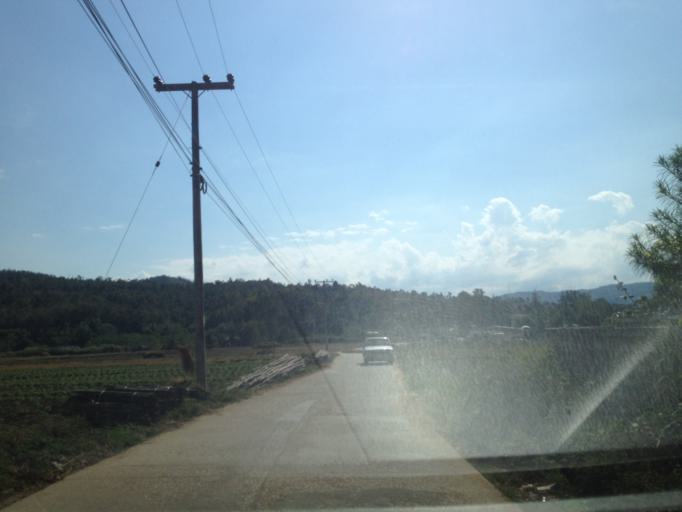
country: TH
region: Mae Hong Son
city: Ban Huai I Huak
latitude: 18.0935
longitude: 98.2044
